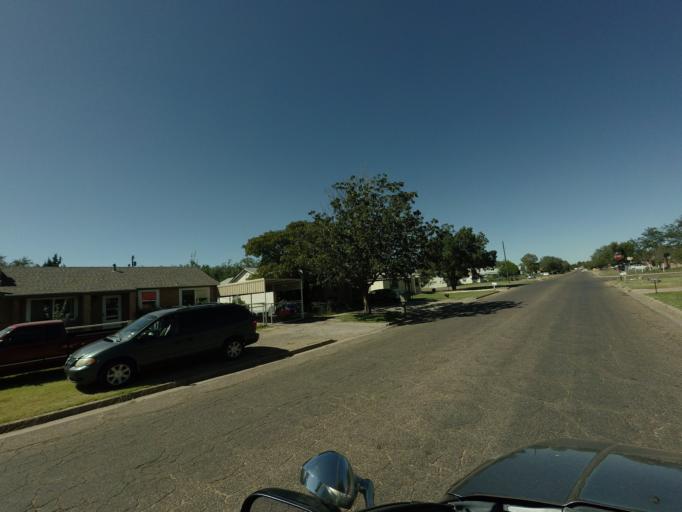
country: US
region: New Mexico
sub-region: Curry County
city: Clovis
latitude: 34.4084
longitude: -103.2205
